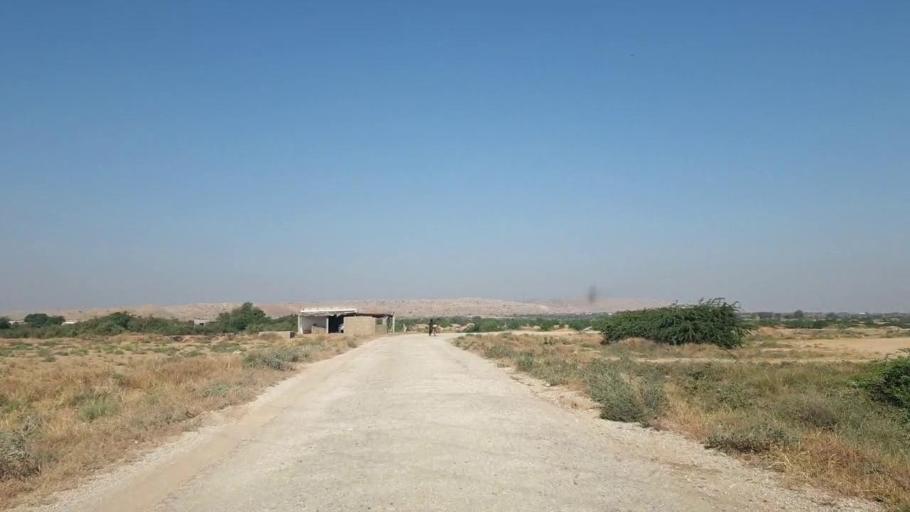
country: PK
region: Sindh
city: Gharo
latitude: 25.1730
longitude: 67.7326
